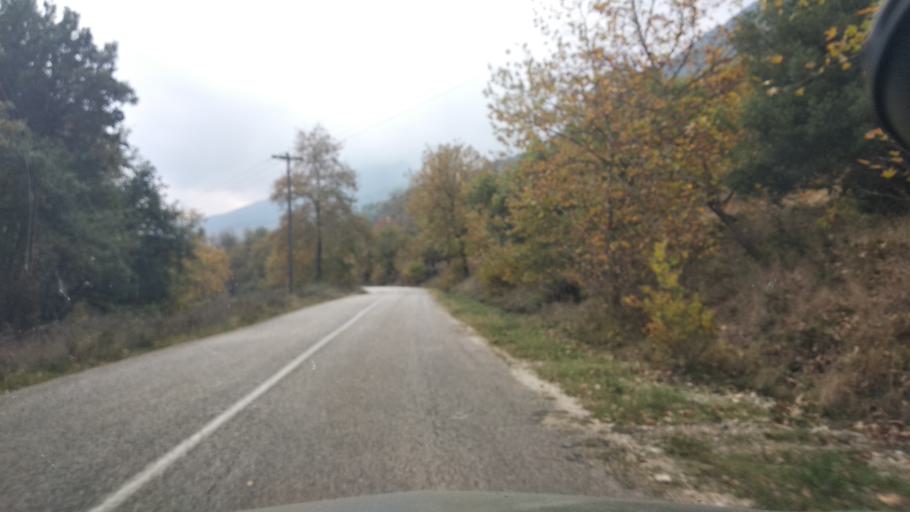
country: GR
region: Thessaly
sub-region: Trikala
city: Kastraki
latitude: 39.6816
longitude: 21.5128
